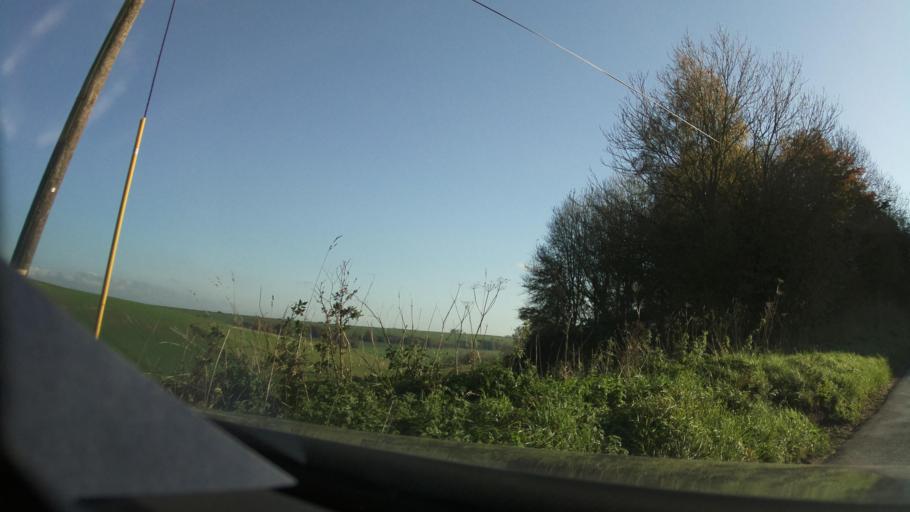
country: GB
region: England
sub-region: Dorset
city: Sherborne
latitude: 50.9894
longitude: -2.5168
